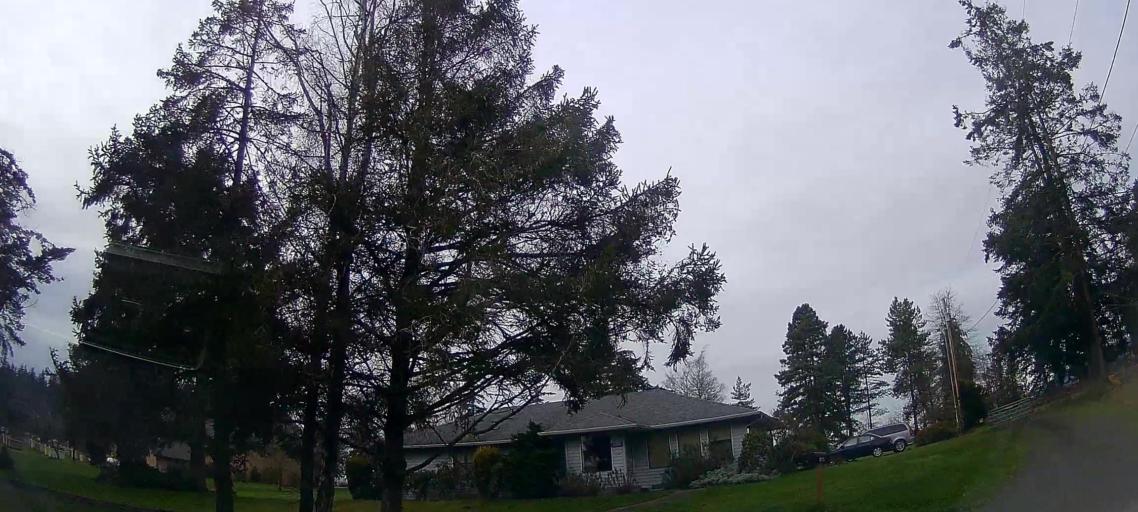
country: US
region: Washington
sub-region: Skagit County
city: Anacortes
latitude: 48.5693
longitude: -122.4905
